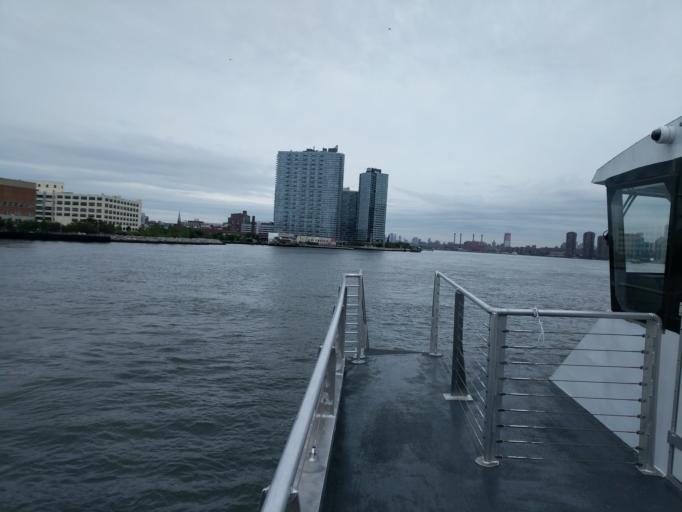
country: US
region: New York
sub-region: Queens County
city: Long Island City
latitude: 40.7541
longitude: -73.9545
